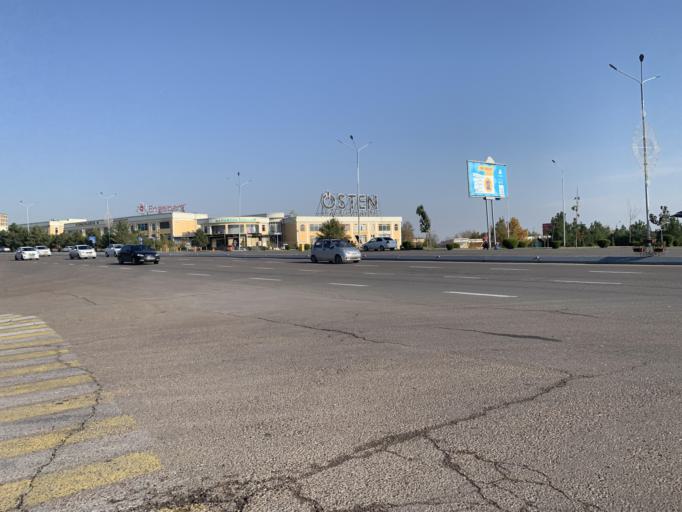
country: UZ
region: Namangan
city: Namangan Shahri
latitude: 40.9969
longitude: 71.5957
